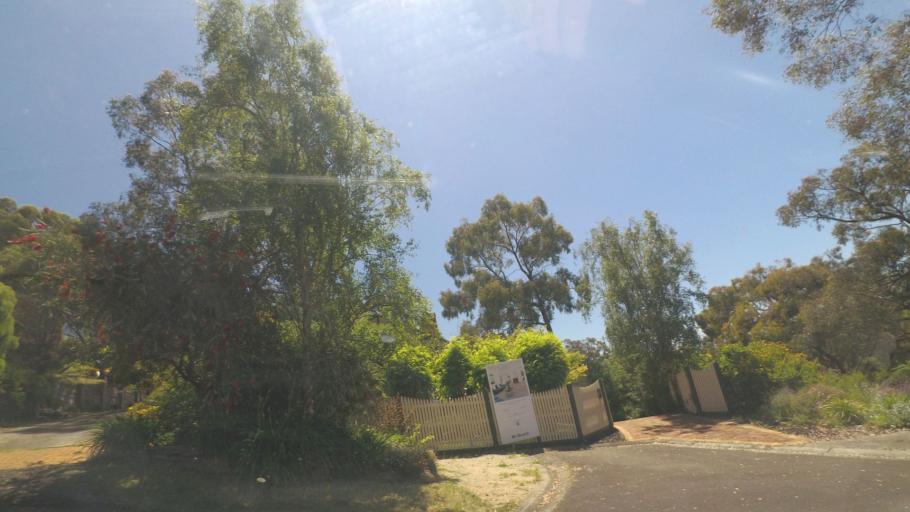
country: AU
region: Victoria
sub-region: Maroondah
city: Croydon North
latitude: -37.7742
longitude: 145.2836
